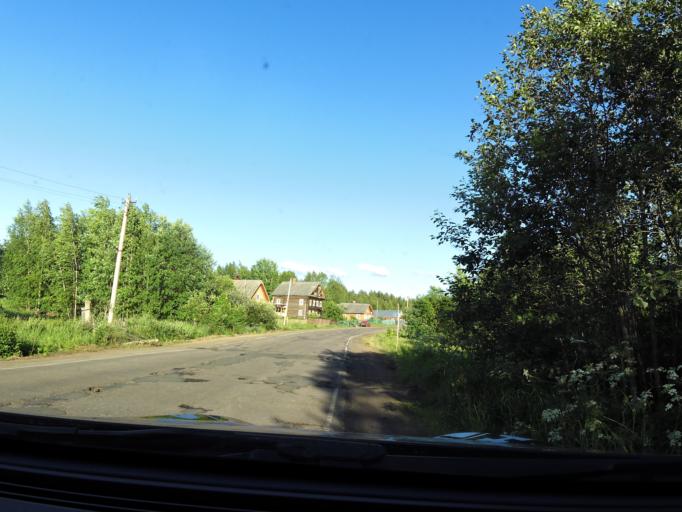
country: RU
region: Republic of Karelia
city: Kvartsitnyy
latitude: 61.4569
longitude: 35.0517
